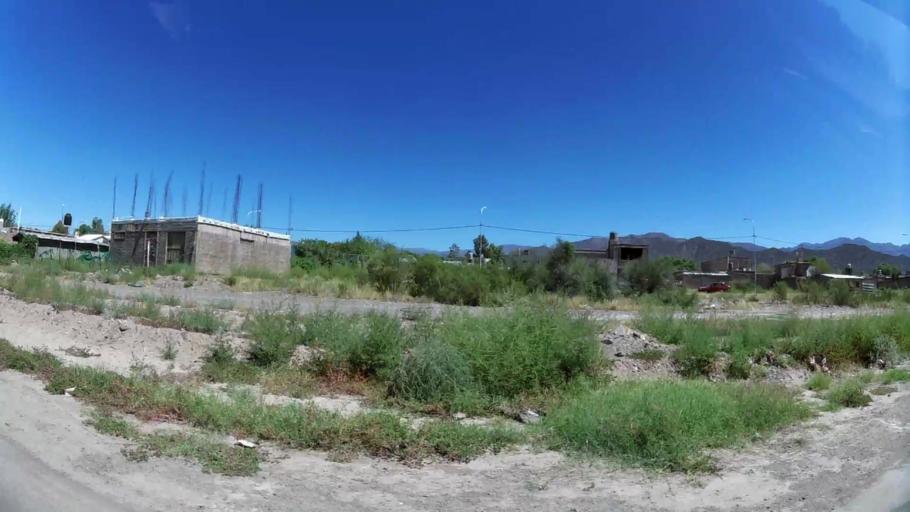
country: AR
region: Mendoza
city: Las Heras
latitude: -32.8422
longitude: -68.8624
